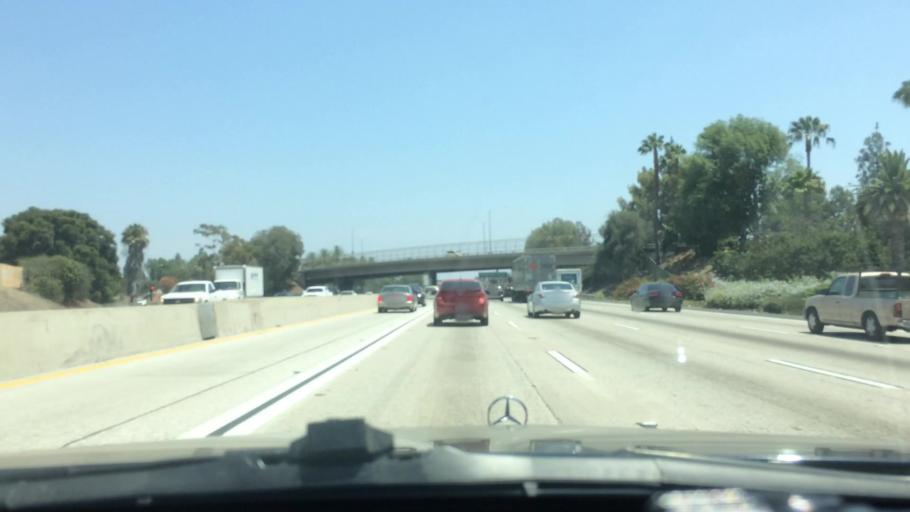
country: US
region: California
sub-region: Los Angeles County
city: Cerritos
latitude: 33.8742
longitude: -118.0618
